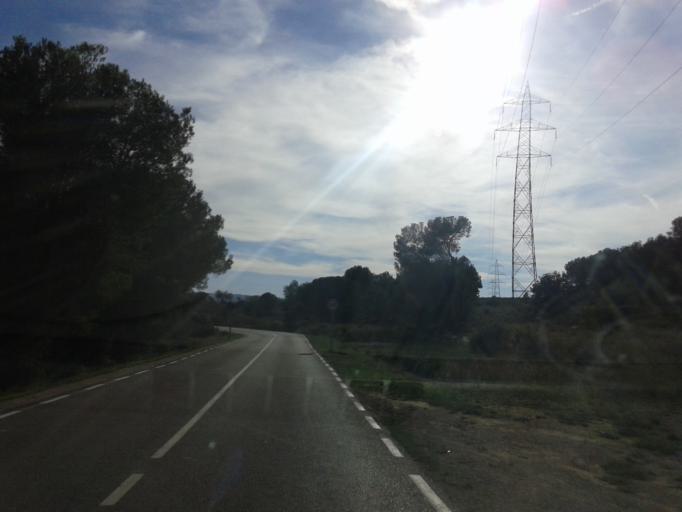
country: ES
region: Catalonia
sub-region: Provincia de Barcelona
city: Vilafranca del Penedes
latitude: 41.3292
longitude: 1.7207
